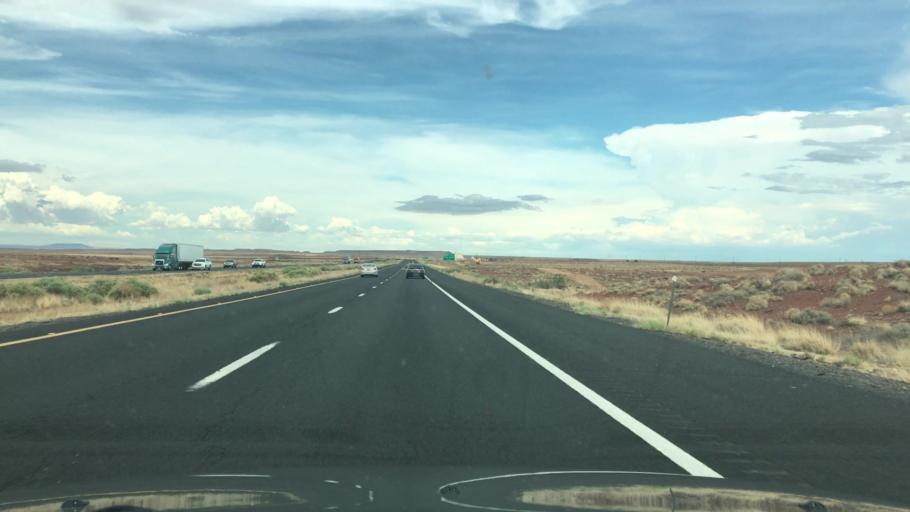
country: US
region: Arizona
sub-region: Coconino County
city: LeChee
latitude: 35.0962
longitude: -110.9475
